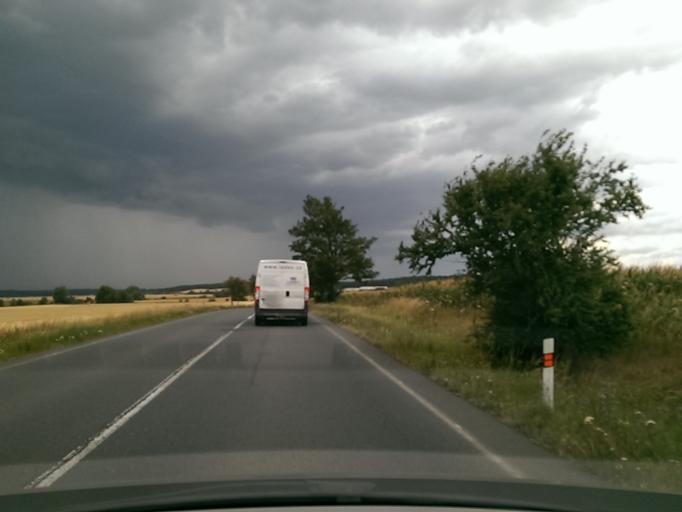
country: CZ
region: Central Bohemia
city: Loucen
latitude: 50.2464
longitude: 15.0071
